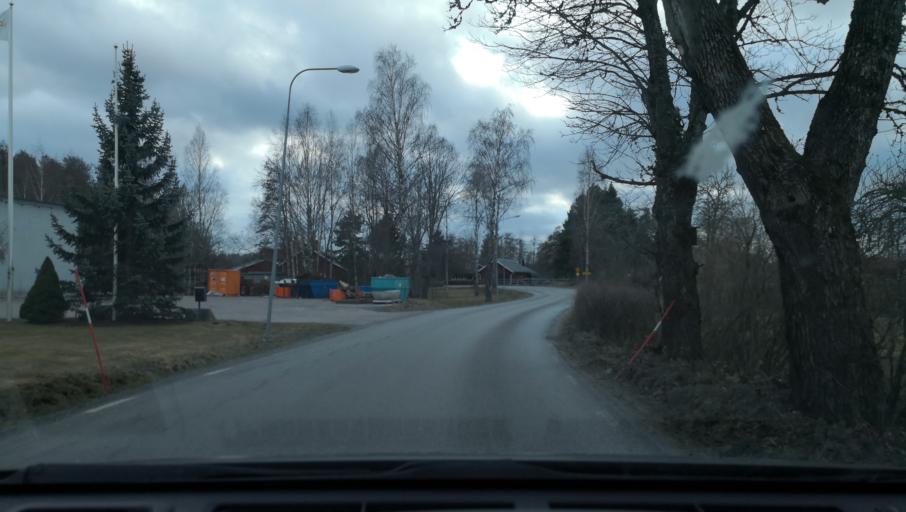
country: SE
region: Vaestmanland
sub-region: Kopings Kommun
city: Koping
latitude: 59.5188
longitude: 15.9199
